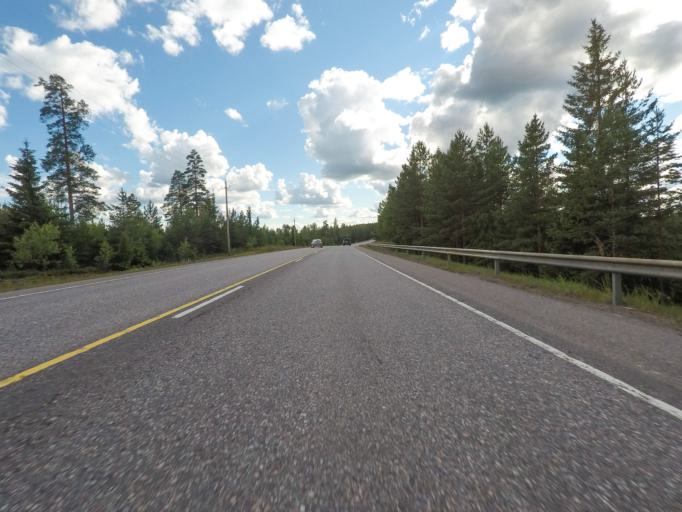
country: FI
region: Uusimaa
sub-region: Helsinki
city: Nurmijaervi
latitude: 60.5150
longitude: 24.6458
